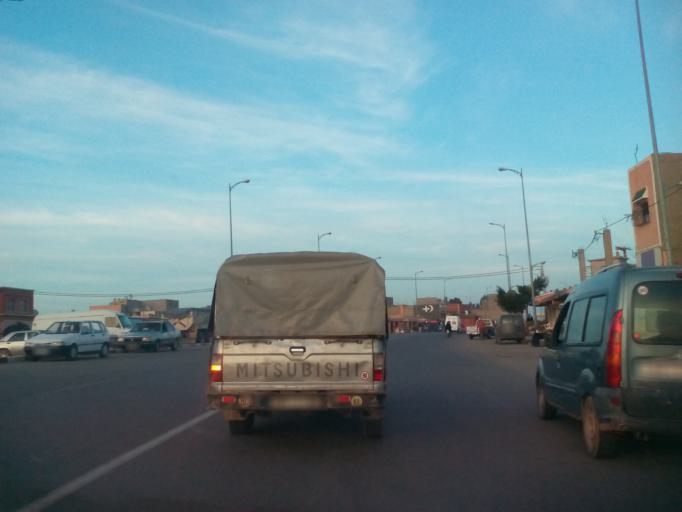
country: MA
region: Marrakech-Tensift-Al Haouz
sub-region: Marrakech
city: Marrakesh
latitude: 31.6340
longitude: -8.2503
